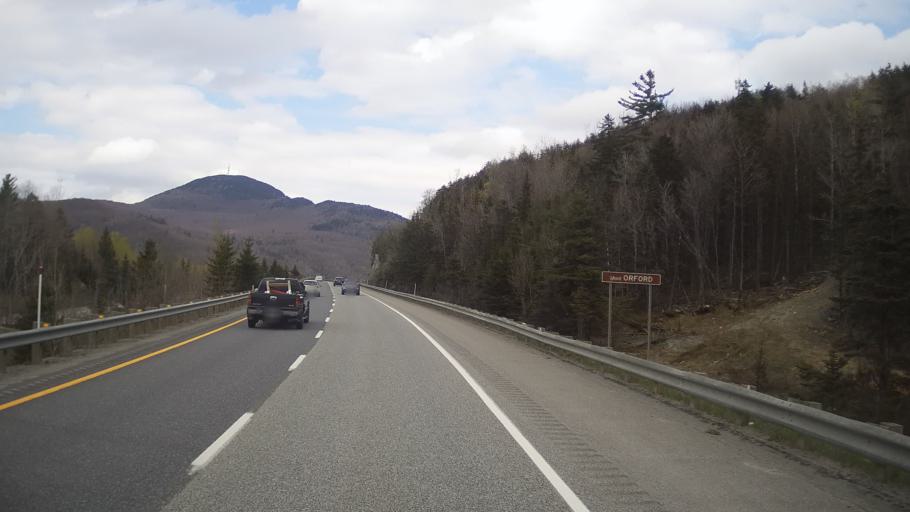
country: CA
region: Quebec
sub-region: Estrie
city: Magog
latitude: 45.2865
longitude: -72.2721
